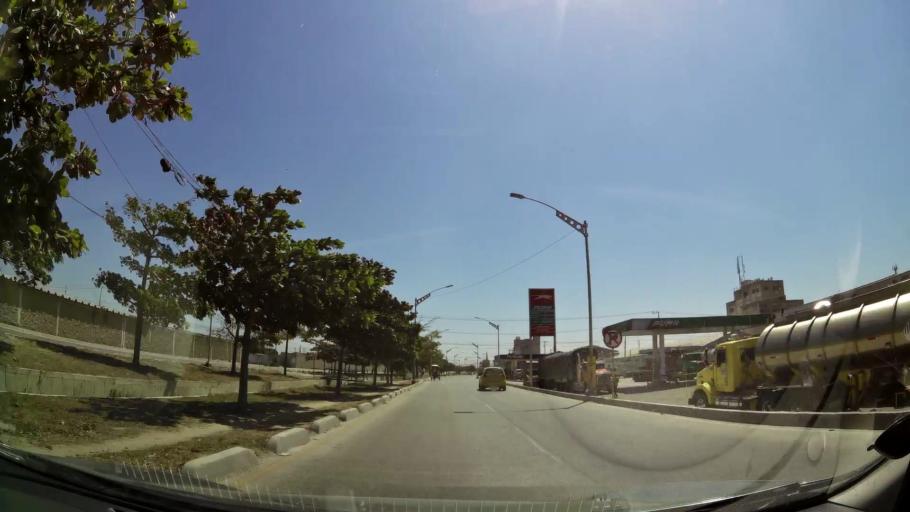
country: CO
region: Atlantico
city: Barranquilla
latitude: 10.9825
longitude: -74.7699
